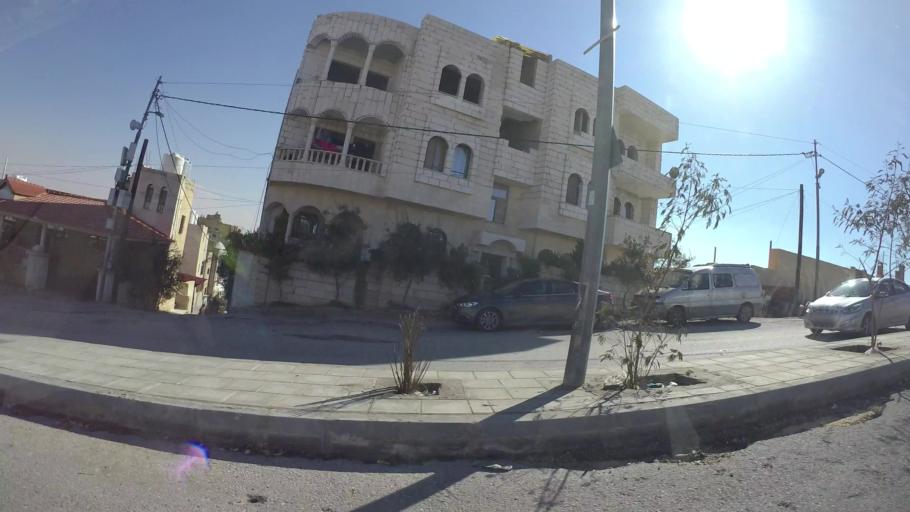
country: JO
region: Zarqa
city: Russeifa
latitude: 32.0419
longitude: 36.0476
